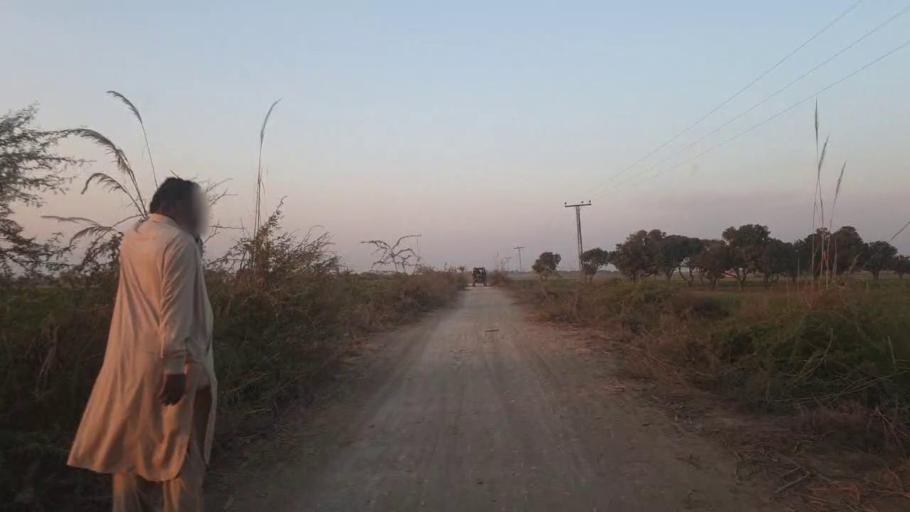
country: PK
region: Sindh
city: Chambar
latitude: 25.3004
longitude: 68.9075
